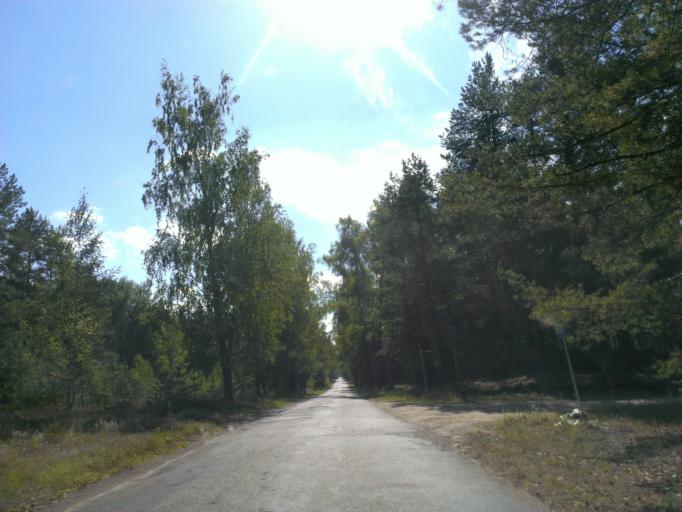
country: LV
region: Adazi
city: Adazi
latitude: 57.1131
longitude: 24.3457
